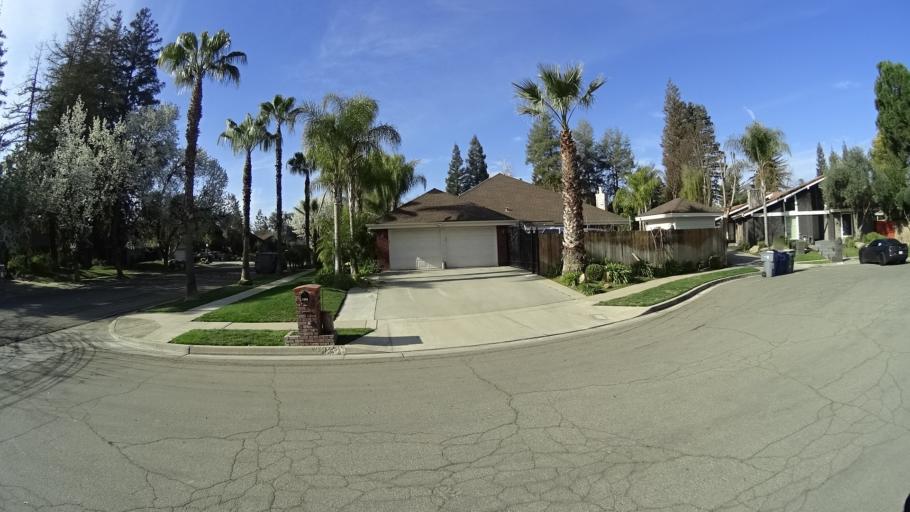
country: US
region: California
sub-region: Fresno County
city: Clovis
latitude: 36.8652
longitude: -119.7709
